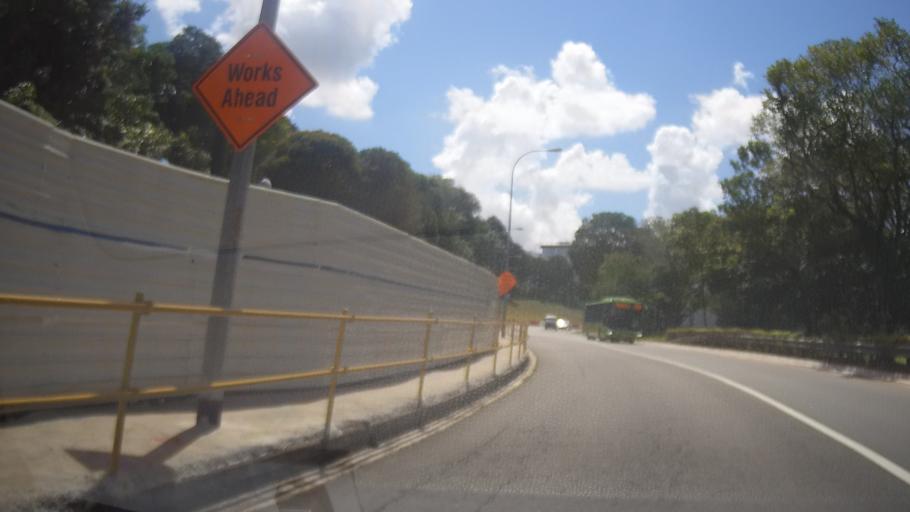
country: MY
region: Johor
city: Johor Bahru
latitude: 1.4355
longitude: 103.7789
